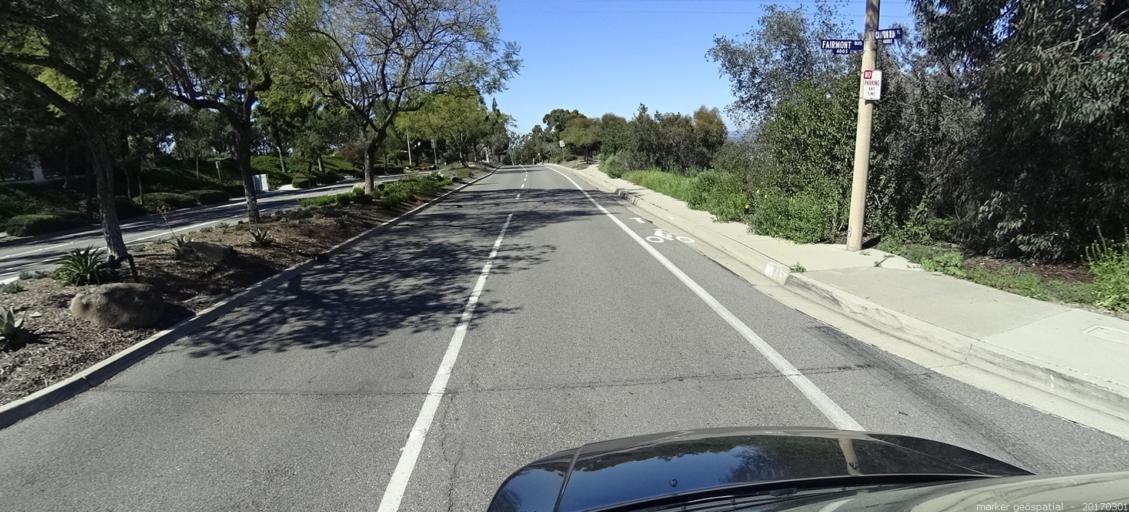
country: US
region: California
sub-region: Orange County
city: Villa Park
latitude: 33.8476
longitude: -117.7577
